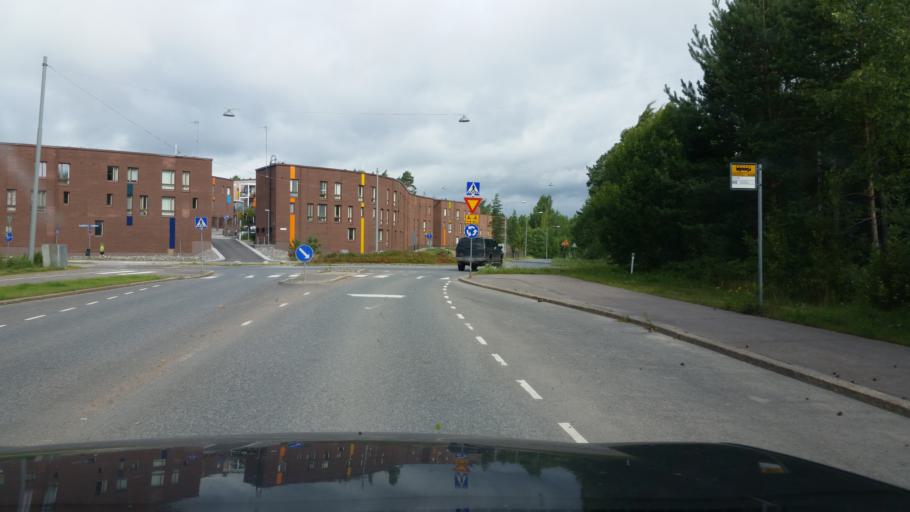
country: FI
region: Uusimaa
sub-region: Helsinki
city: Vantaa
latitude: 60.2247
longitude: 25.1385
